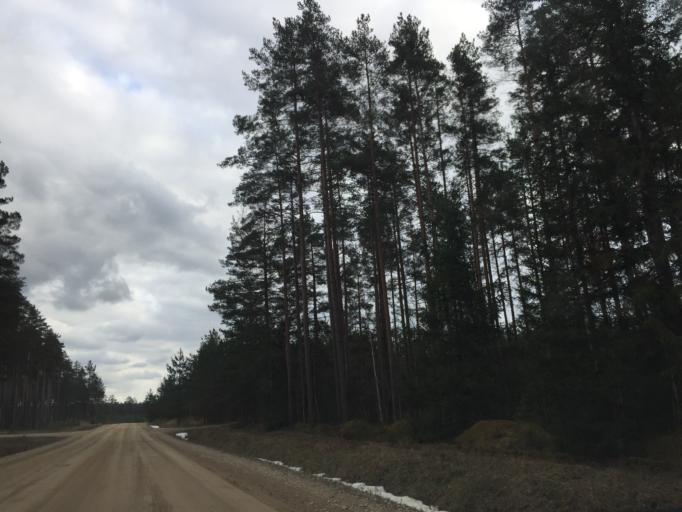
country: LV
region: Jaunjelgava
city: Jaunjelgava
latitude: 56.5840
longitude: 25.0027
